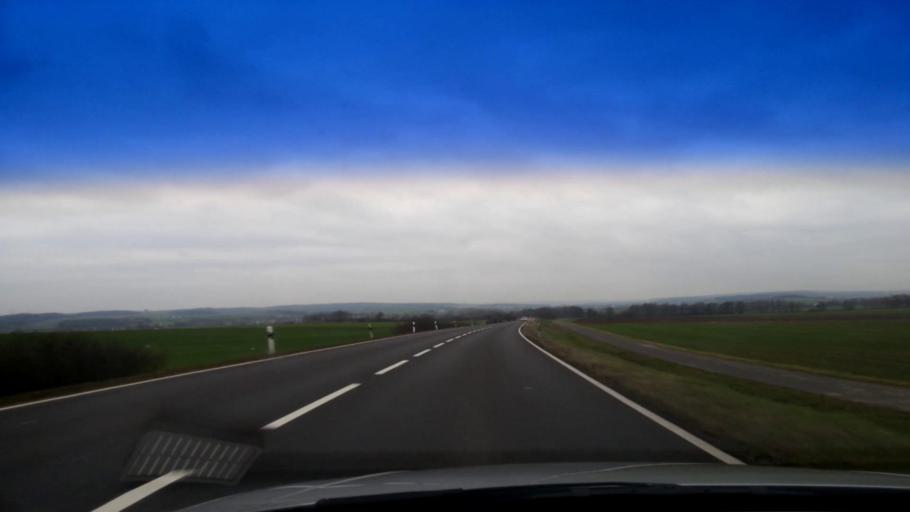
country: DE
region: Bavaria
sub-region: Upper Franconia
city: Walsdorf
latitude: 49.8333
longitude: 10.8088
